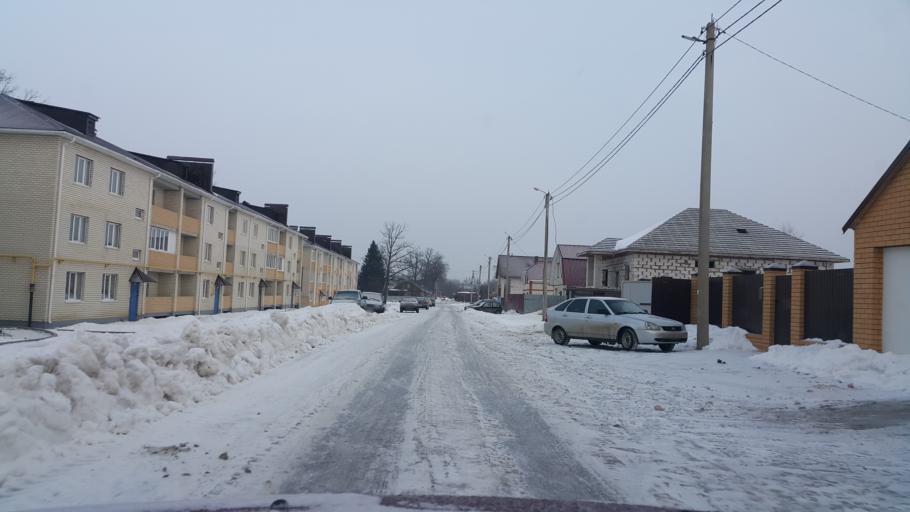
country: RU
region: Tambov
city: Kotovsk
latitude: 52.5747
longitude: 41.5218
